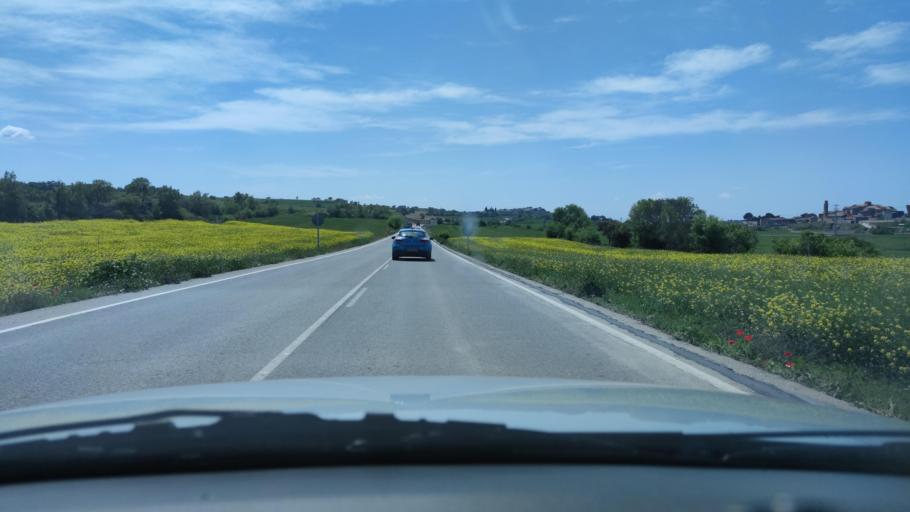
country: ES
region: Catalonia
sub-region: Provincia de Lleida
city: Mont-roig del Camp
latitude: 41.7767
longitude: 1.2668
